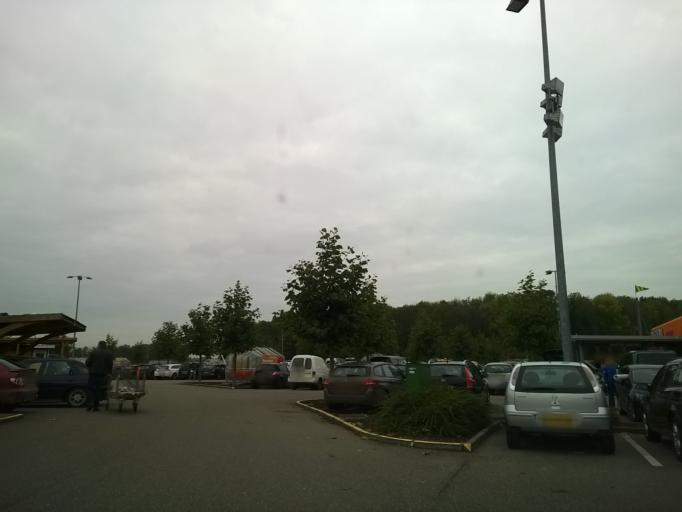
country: NL
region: Groningen
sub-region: Gemeente Groningen
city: Korrewegwijk
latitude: 53.2509
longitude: 6.5805
